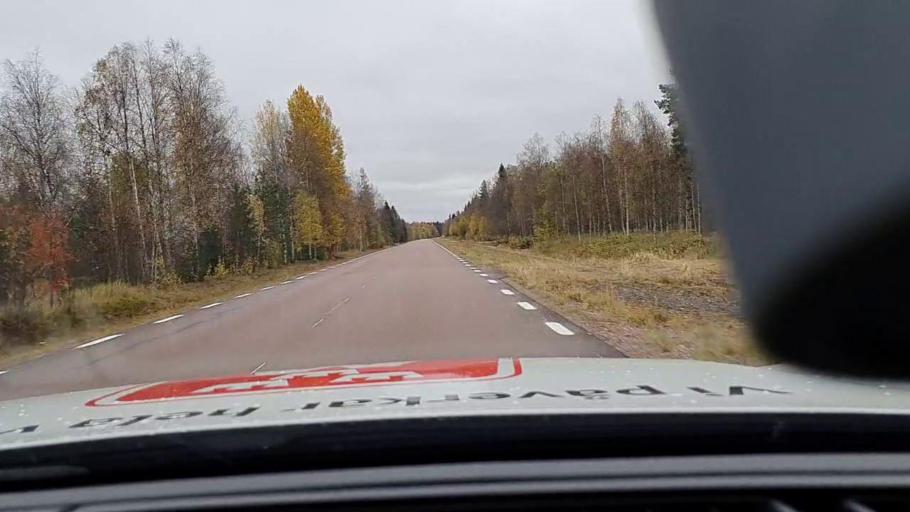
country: FI
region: Lapland
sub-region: Kemi-Tornio
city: Tornio
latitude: 66.0548
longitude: 23.9355
